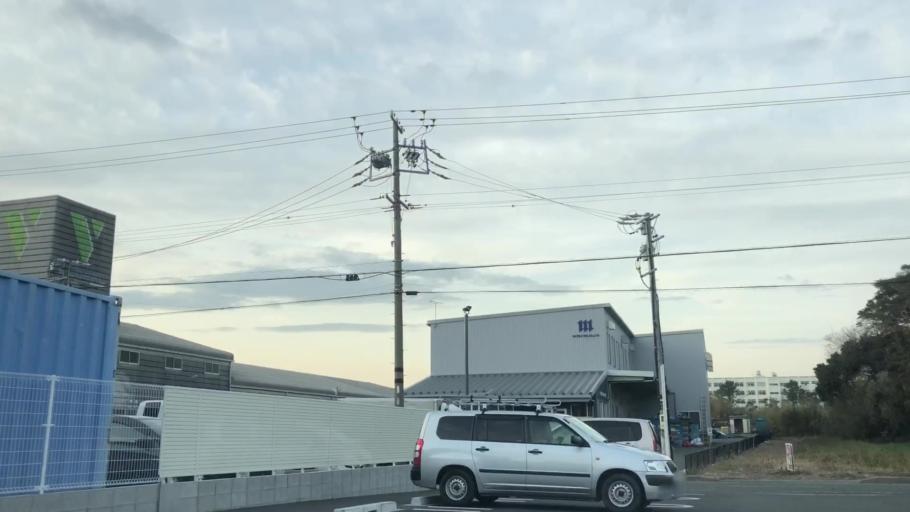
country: JP
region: Aichi
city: Toyohashi
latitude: 34.7197
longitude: 137.4092
